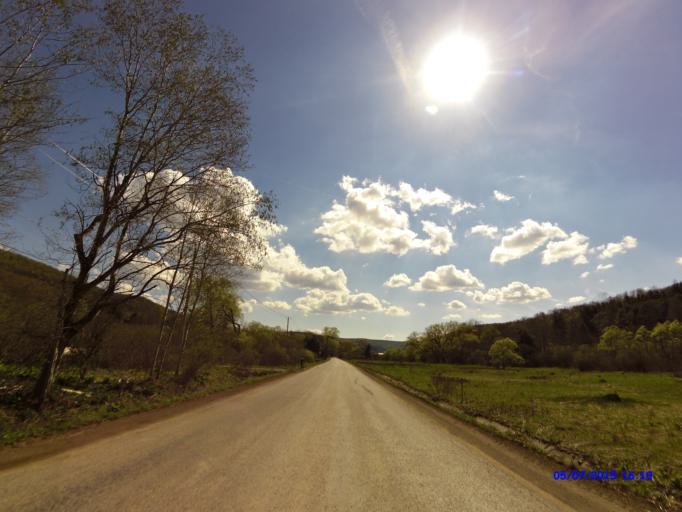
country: US
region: New York
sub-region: Cattaraugus County
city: Salamanca
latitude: 42.2687
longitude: -78.6246
